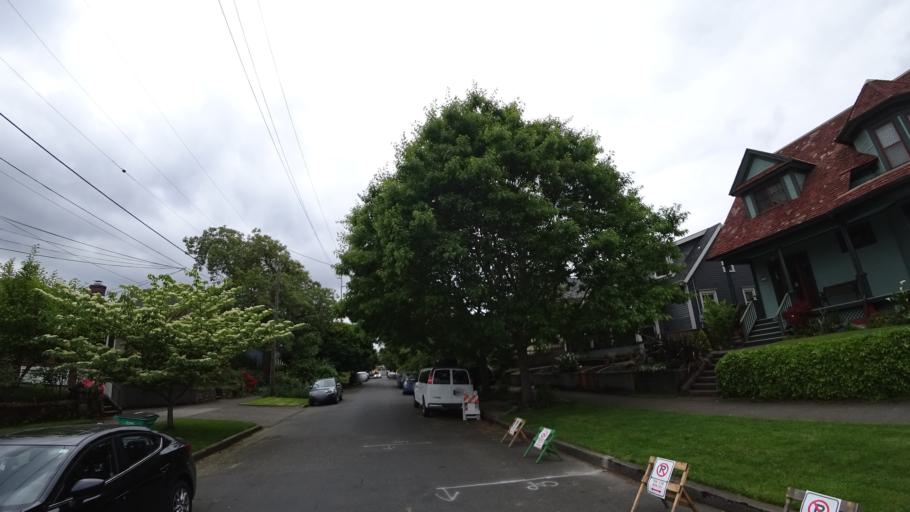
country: US
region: Oregon
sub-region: Multnomah County
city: Portland
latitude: 45.5158
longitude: -122.6196
